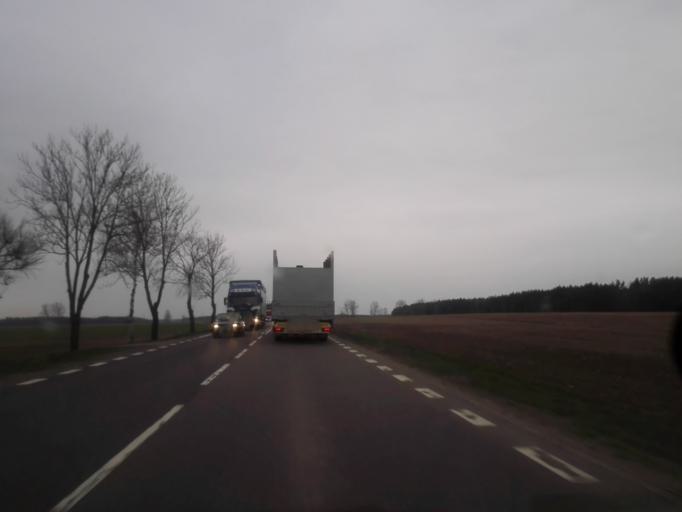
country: PL
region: Podlasie
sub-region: Powiat grajewski
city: Grajewo
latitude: 53.6068
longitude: 22.3706
